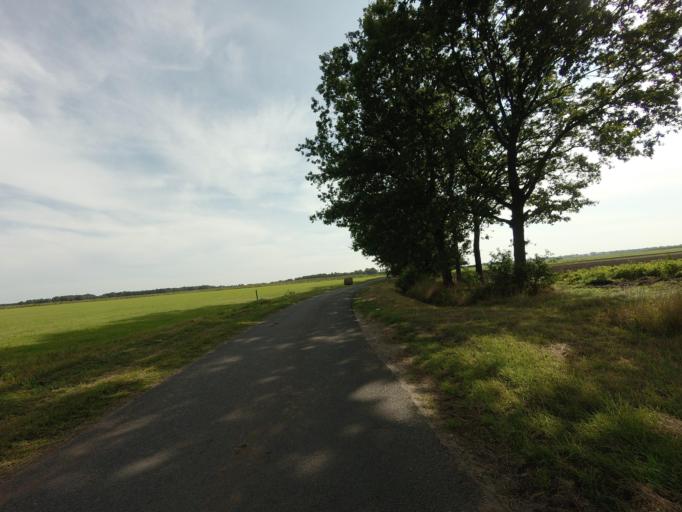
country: NL
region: Drenthe
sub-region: Gemeente Coevorden
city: Dalen
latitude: 52.7148
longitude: 6.7304
